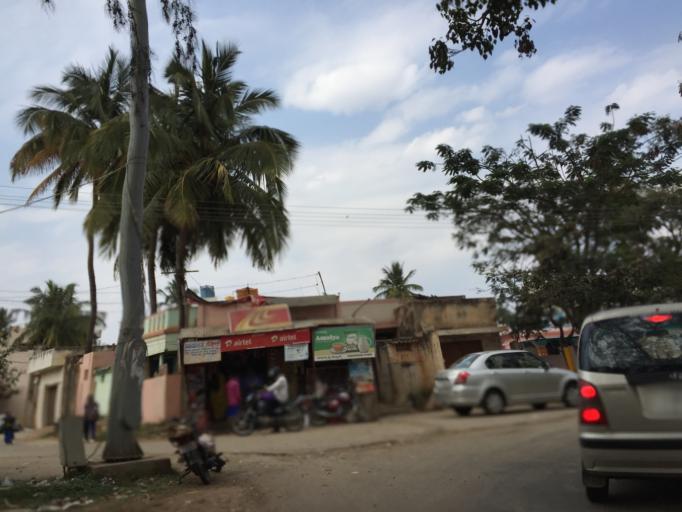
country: IN
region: Karnataka
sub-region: Chikkaballapur
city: Chik Ballapur
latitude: 13.4280
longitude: 77.7230
